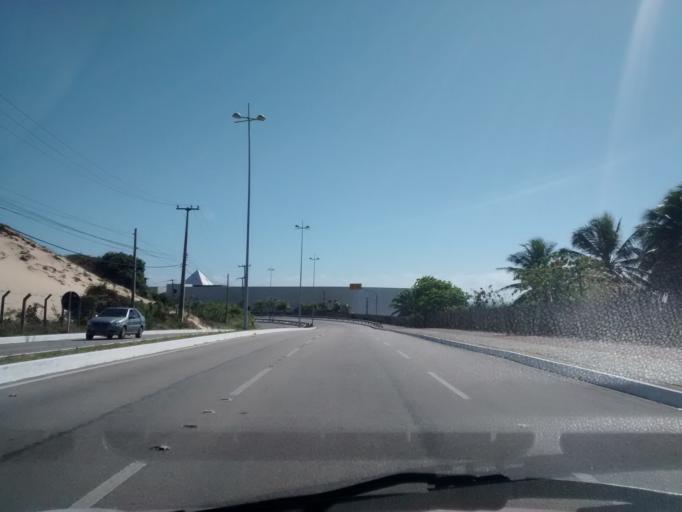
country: BR
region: Rio Grande do Norte
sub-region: Natal
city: Natal
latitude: -5.8066
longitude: -35.1826
